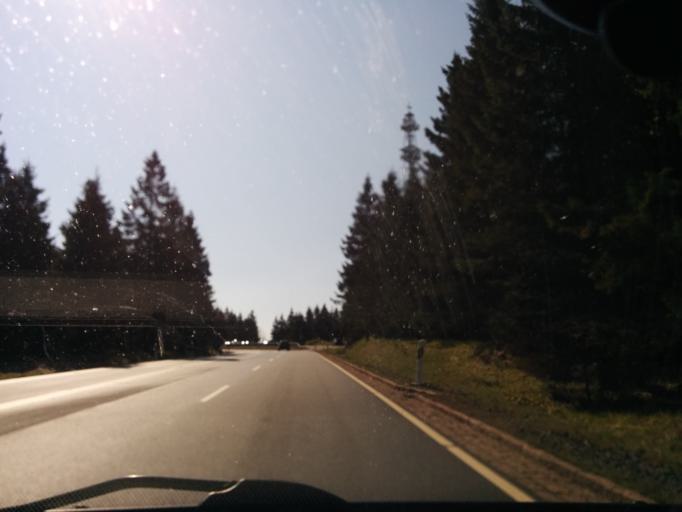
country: DE
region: Lower Saxony
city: Altenau
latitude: 51.7706
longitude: 10.4544
